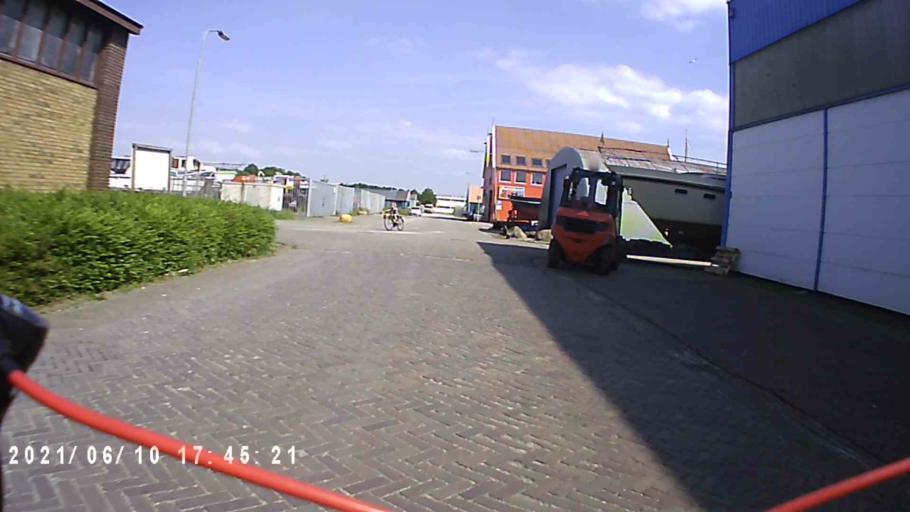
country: NL
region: Groningen
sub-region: Gemeente De Marne
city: Ulrum
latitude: 53.3359
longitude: 6.3017
